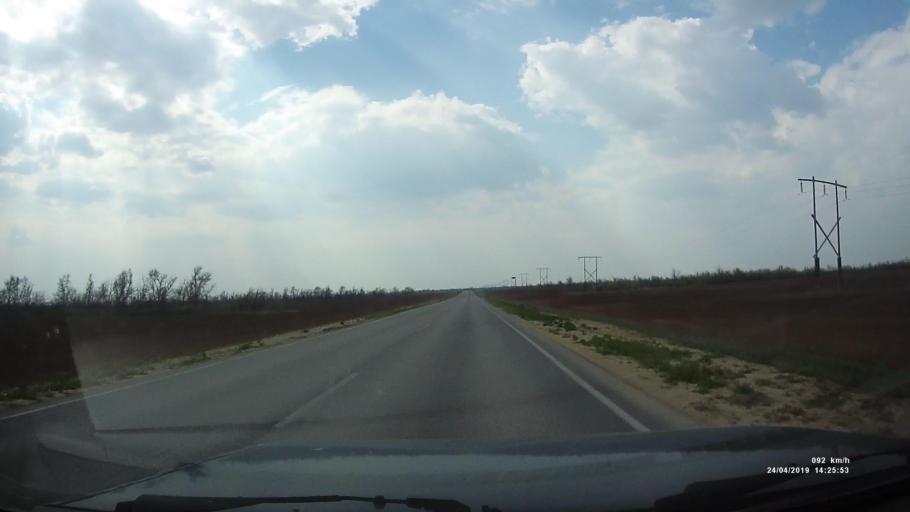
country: RU
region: Kalmykiya
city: Arshan'
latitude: 46.3320
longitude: 44.0735
